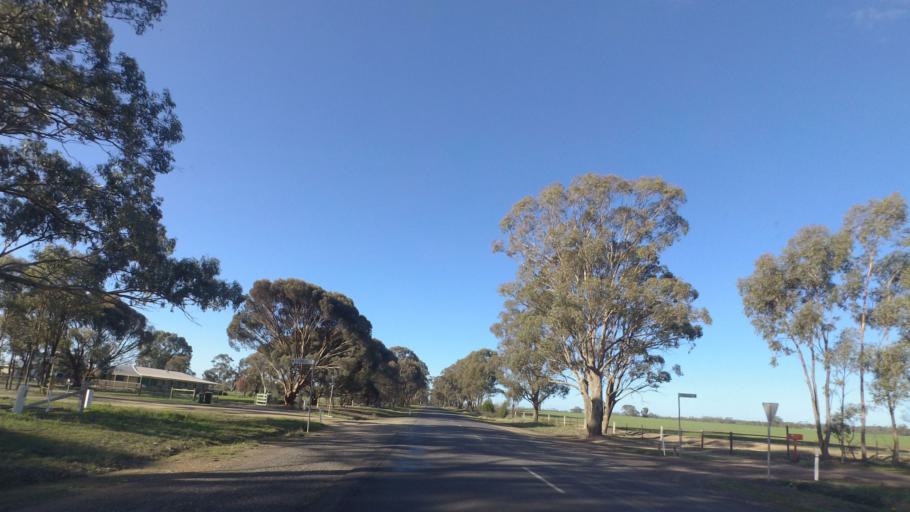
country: AU
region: Victoria
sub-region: Greater Bendigo
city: Epsom
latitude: -36.6594
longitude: 144.4704
